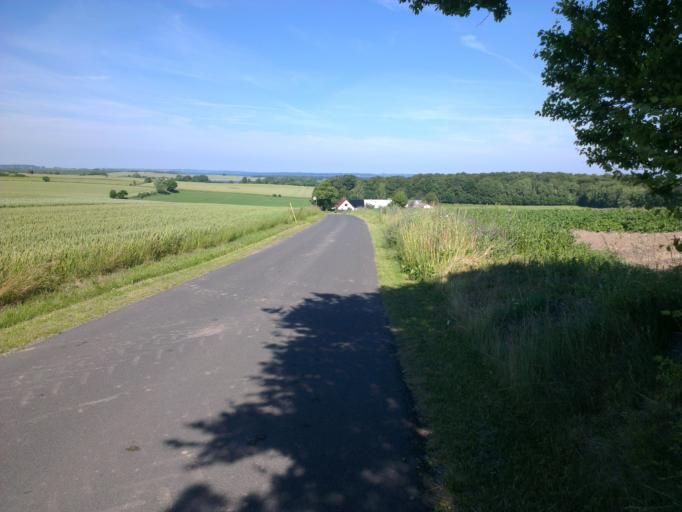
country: DK
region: Capital Region
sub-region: Frederikssund Kommune
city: Skibby
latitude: 55.7839
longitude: 11.8841
